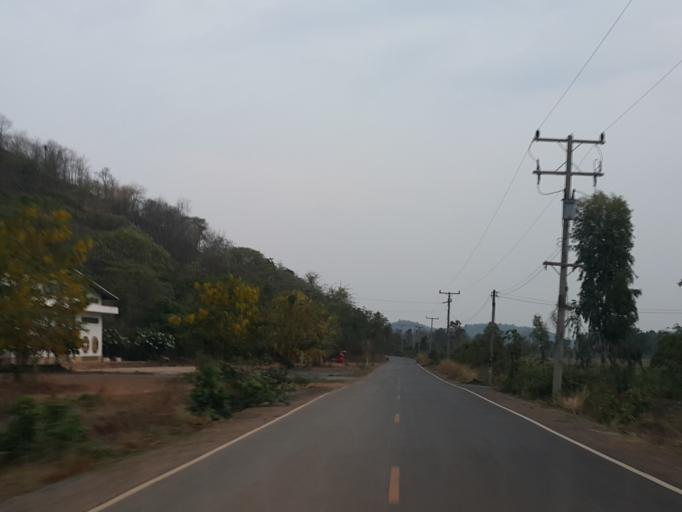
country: TH
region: Suphan Buri
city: Dan Chang
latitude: 14.8738
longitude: 99.6629
